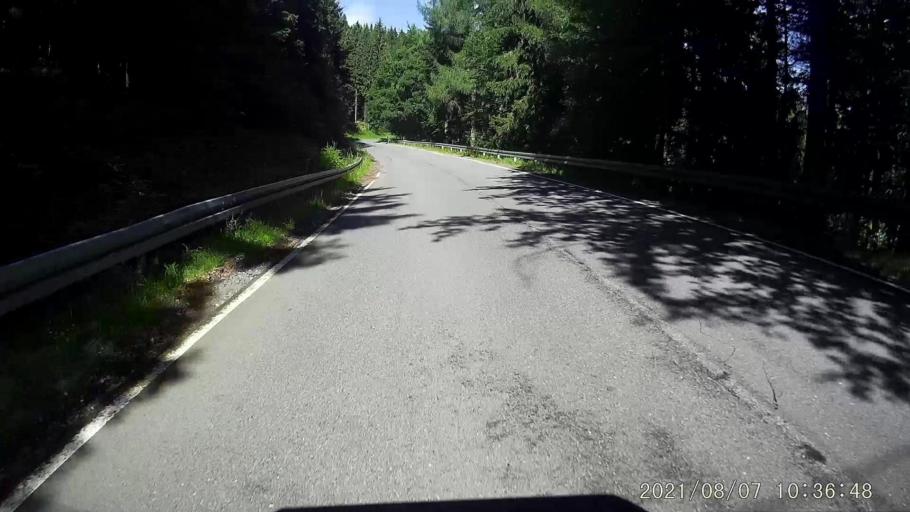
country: PL
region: Lower Silesian Voivodeship
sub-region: Powiat klodzki
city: Duszniki-Zdroj
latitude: 50.3602
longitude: 16.3726
